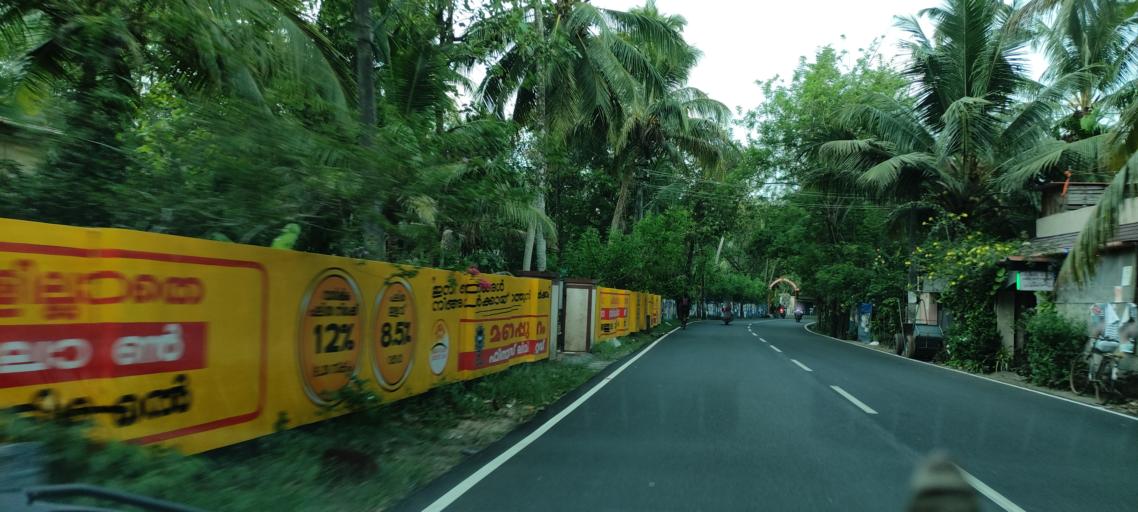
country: IN
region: Kerala
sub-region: Alappuzha
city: Kutiatodu
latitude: 9.8216
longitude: 76.3453
